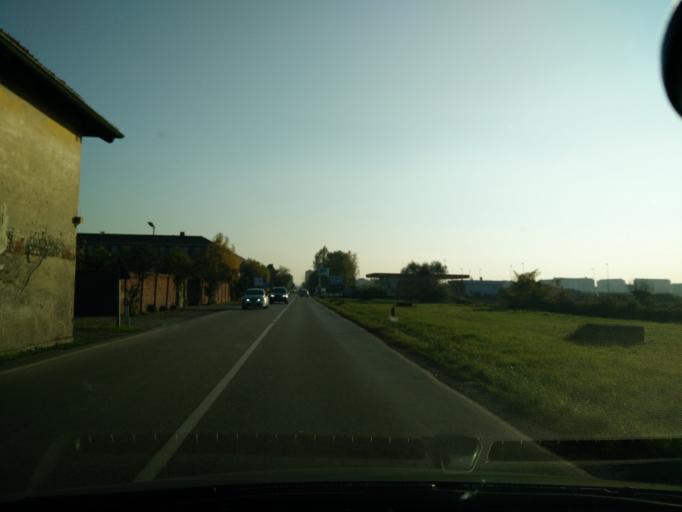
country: IT
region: Piedmont
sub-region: Provincia di Torino
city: Leini
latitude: 45.1581
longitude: 7.7100
